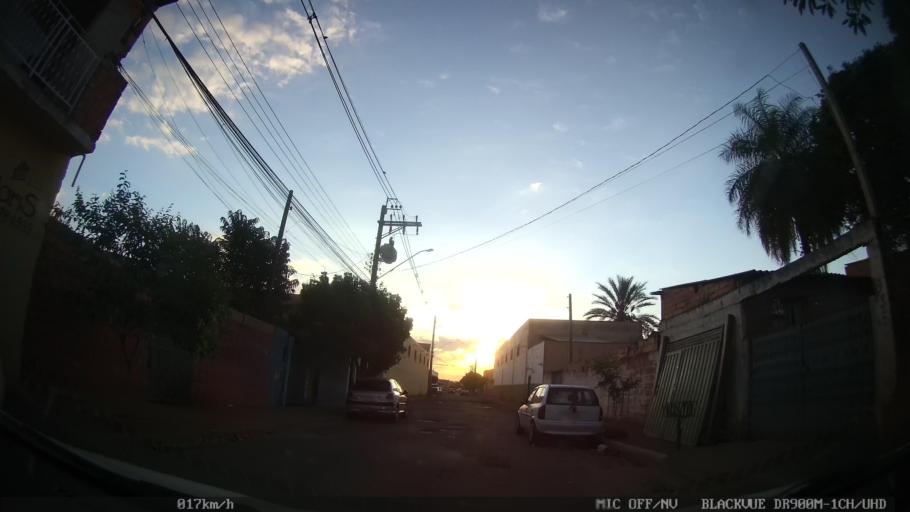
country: BR
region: Sao Paulo
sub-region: Ribeirao Preto
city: Ribeirao Preto
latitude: -21.1450
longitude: -47.7915
